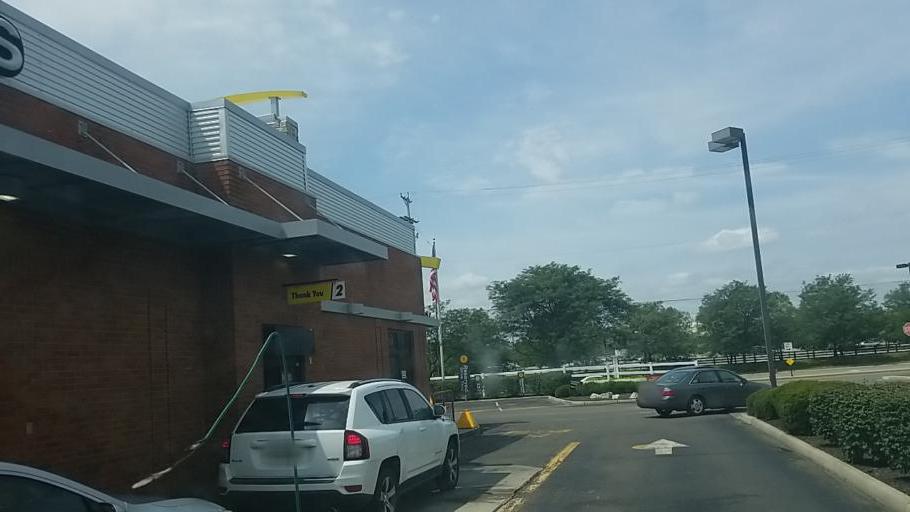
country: US
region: Ohio
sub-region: Franklin County
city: Gahanna
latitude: 40.0563
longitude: -82.8628
